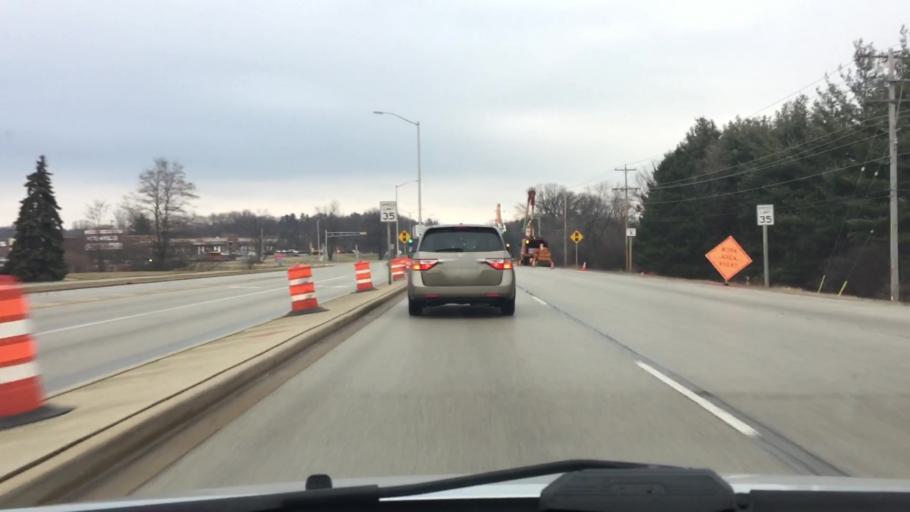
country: US
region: Wisconsin
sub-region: Waukesha County
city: Waukesha
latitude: 42.9889
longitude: -88.2666
